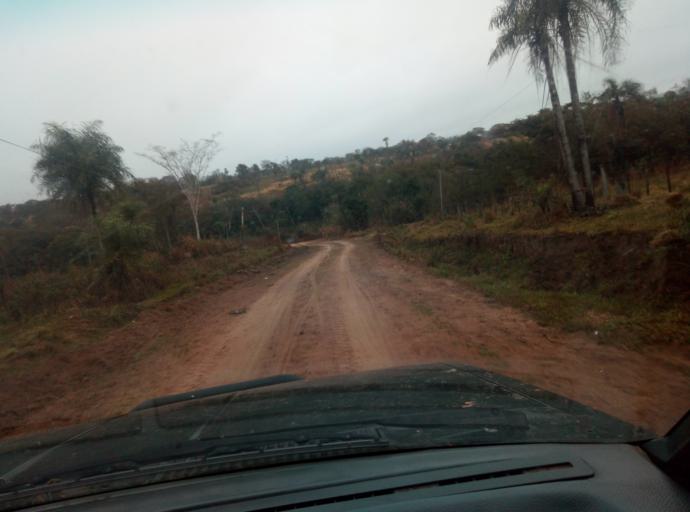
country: PY
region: Caaguazu
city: Carayao
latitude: -25.1935
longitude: -56.3216
